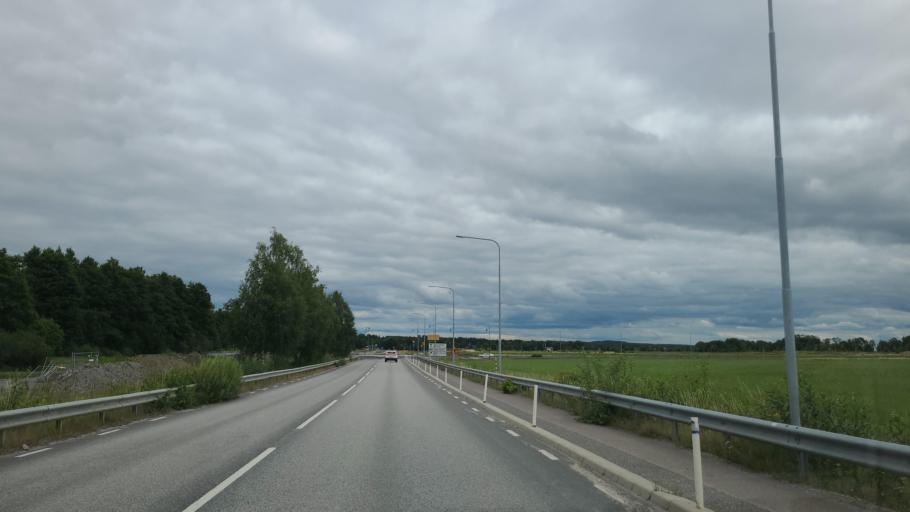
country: SE
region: Stockholm
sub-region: Upplands-Bro Kommun
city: Bro
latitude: 59.5109
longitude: 17.6266
